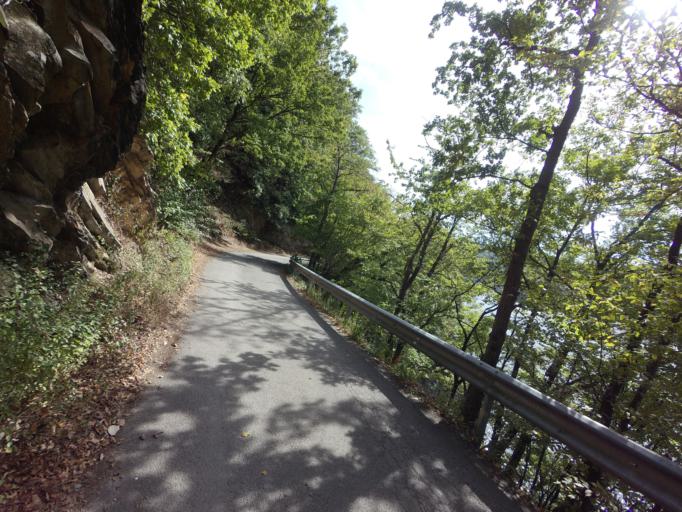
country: DE
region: North Rhine-Westphalia
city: Heimbach
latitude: 50.6345
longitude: 6.3986
